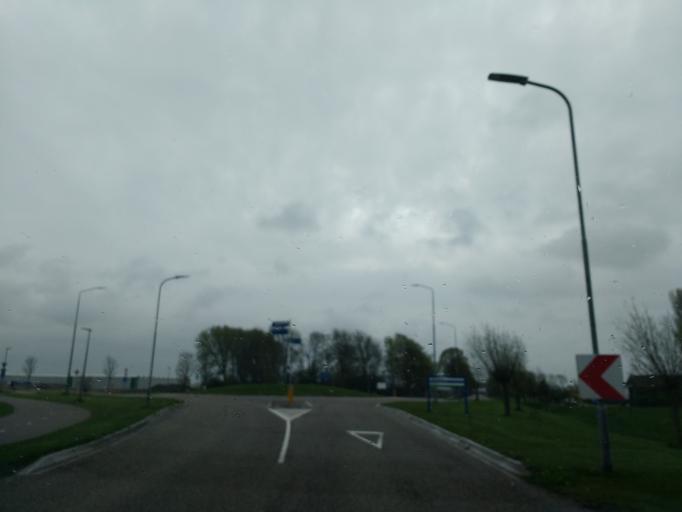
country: NL
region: North Holland
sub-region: Gemeente Schagen
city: Harenkarspel
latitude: 52.7153
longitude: 4.7267
